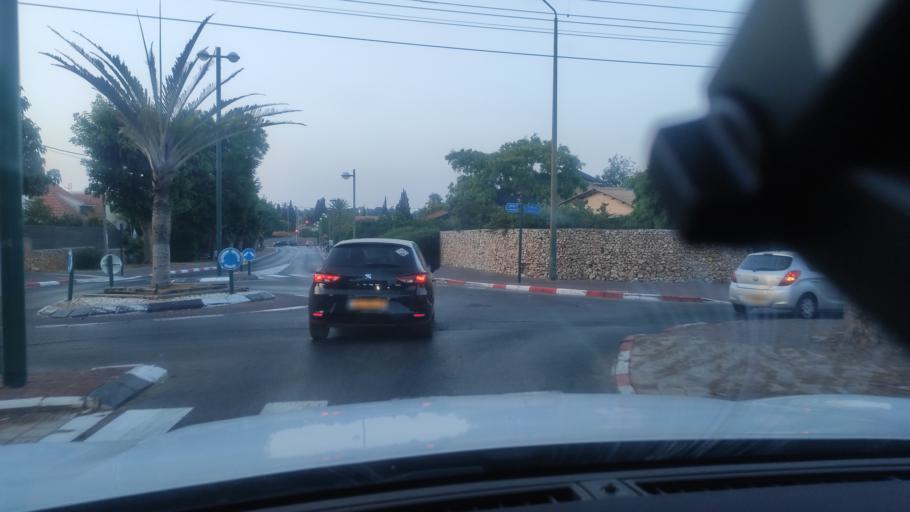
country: IL
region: Central District
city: Kfar Saba
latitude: 32.1848
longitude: 34.9051
